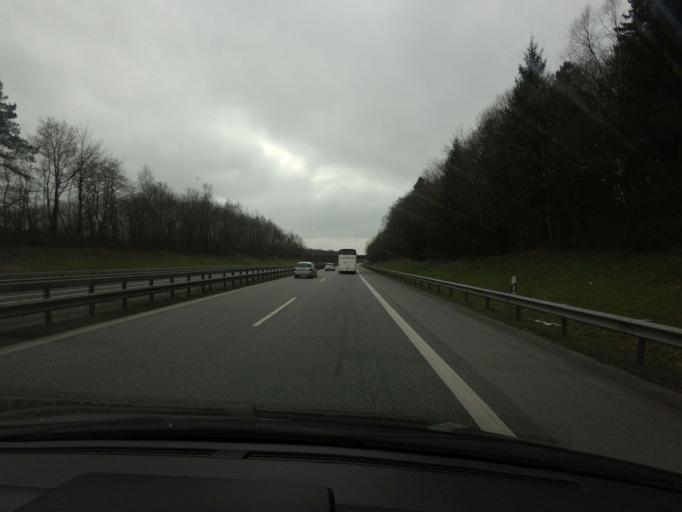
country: DE
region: Lower Saxony
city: Seevetal
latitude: 53.4288
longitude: 9.9280
